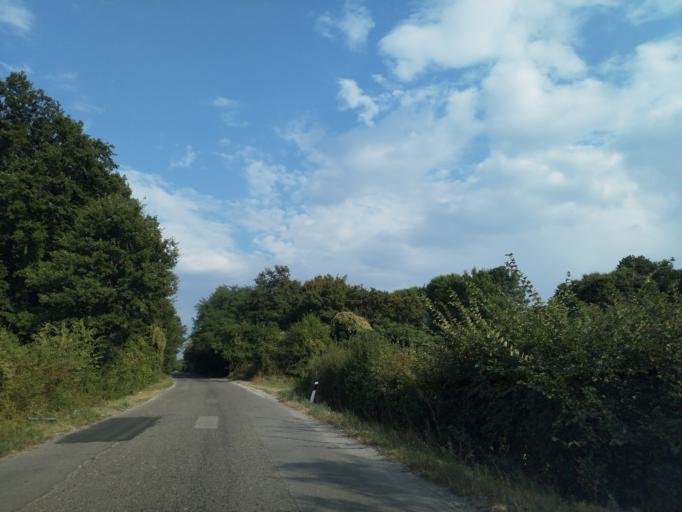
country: RS
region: Central Serbia
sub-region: Pomoravski Okrug
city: Paracin
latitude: 43.8491
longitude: 21.4519
